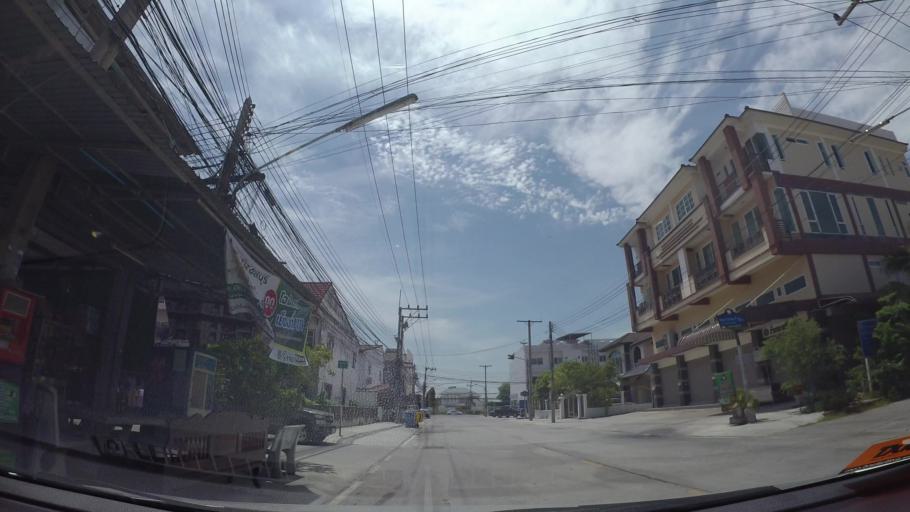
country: TH
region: Chon Buri
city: Chon Buri
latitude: 13.3349
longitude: 100.9503
